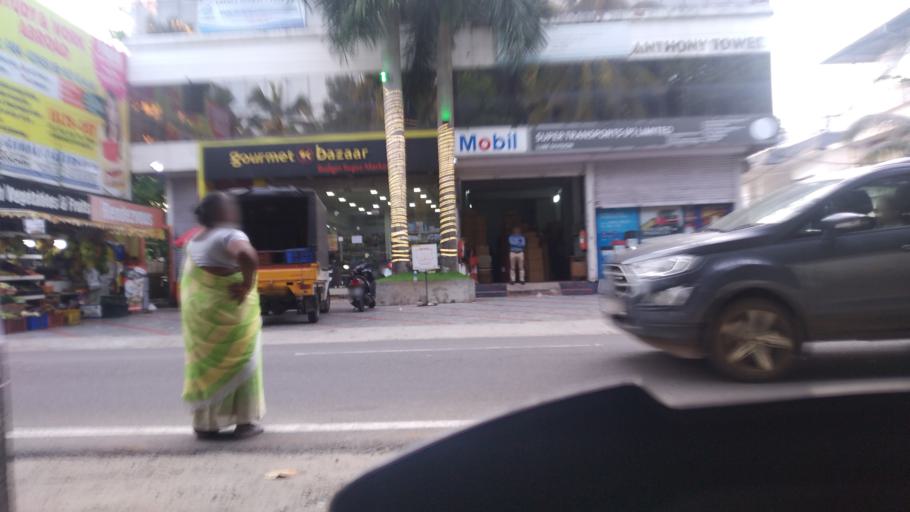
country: IN
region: Kerala
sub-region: Ernakulam
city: Elur
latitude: 10.0042
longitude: 76.2897
